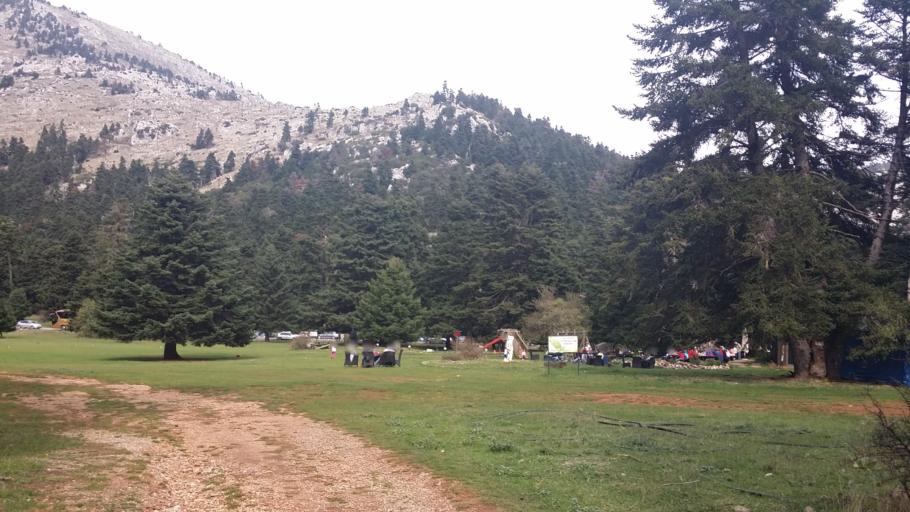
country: GR
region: Central Greece
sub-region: Nomos Voiotias
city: Ayia Trias
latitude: 38.3211
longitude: 22.8544
